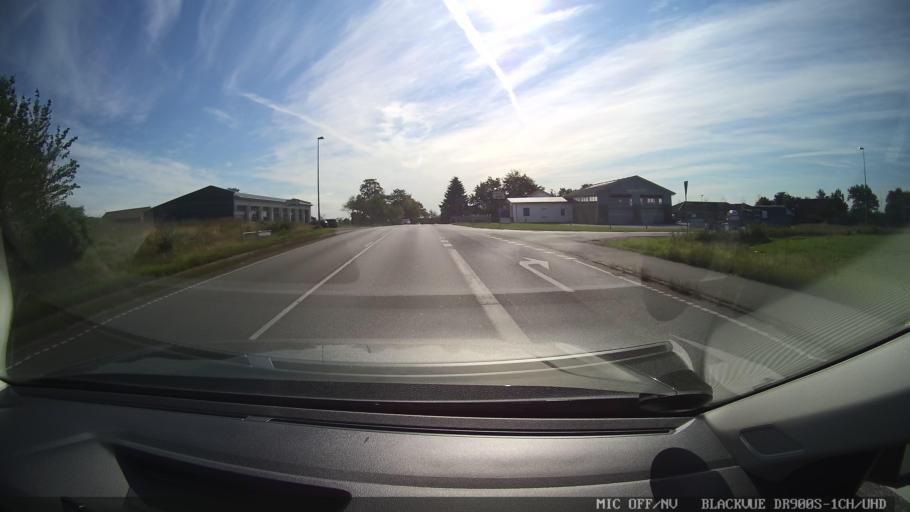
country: DK
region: North Denmark
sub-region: Mariagerfjord Kommune
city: Arden
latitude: 56.7717
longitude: 9.8498
